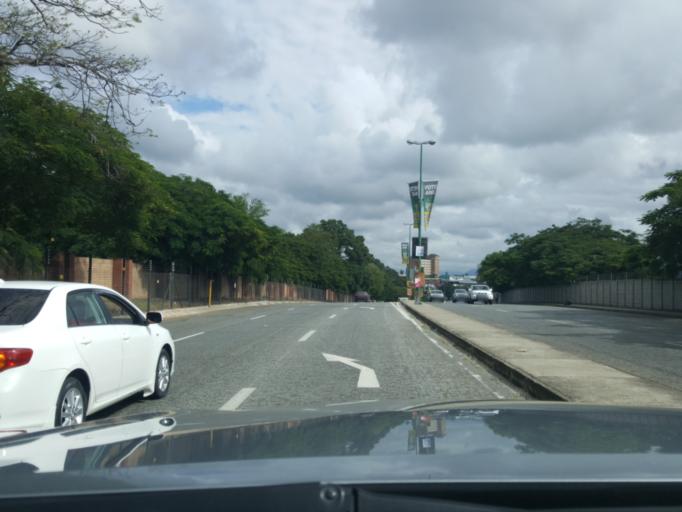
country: ZA
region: Mpumalanga
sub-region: Ehlanzeni District
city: Nelspruit
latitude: -25.4706
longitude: 30.9879
